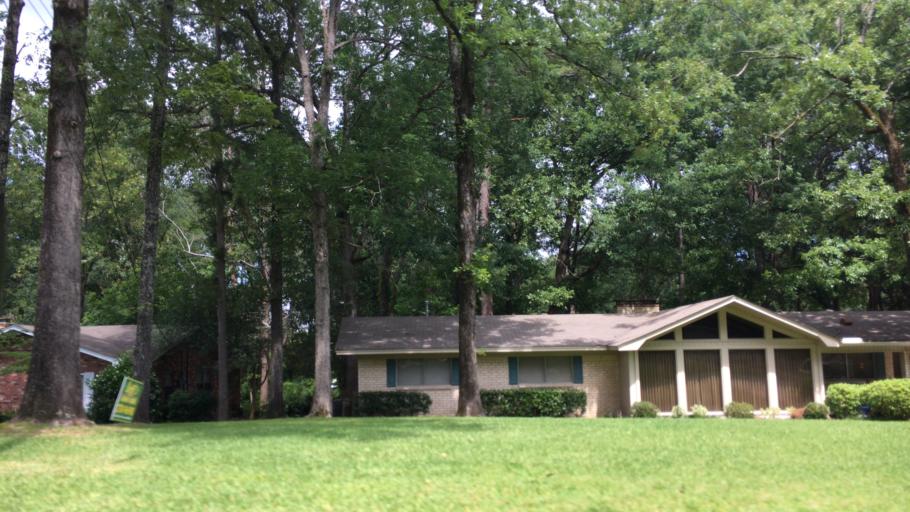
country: US
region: Louisiana
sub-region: Lincoln Parish
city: Ruston
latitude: 32.5503
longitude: -92.6387
